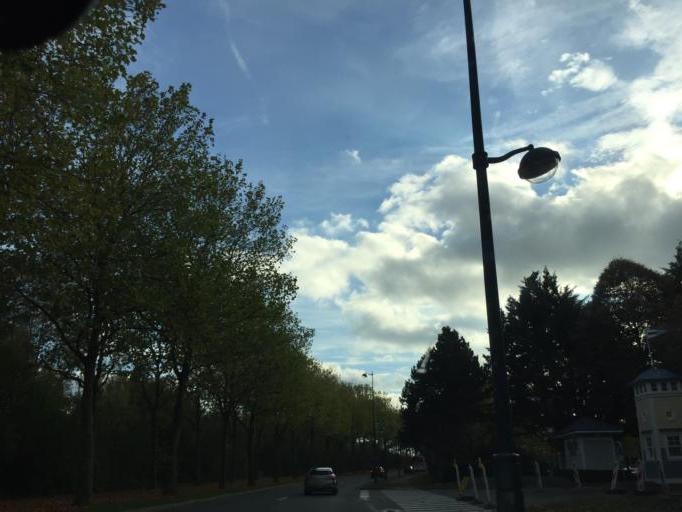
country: FR
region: Ile-de-France
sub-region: Departement de Seine-et-Marne
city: Serris
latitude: 48.8650
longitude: 2.7914
